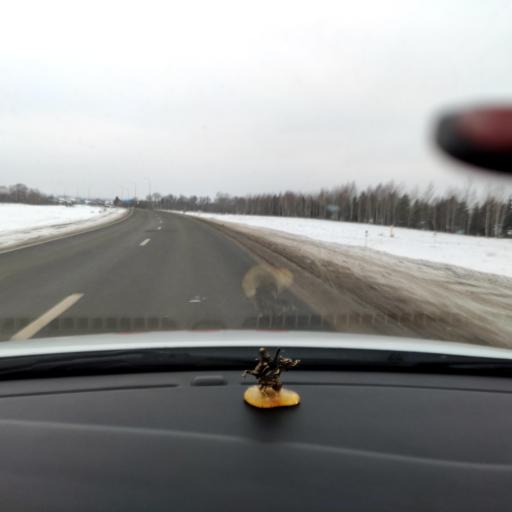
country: RU
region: Tatarstan
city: Stolbishchi
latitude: 55.6303
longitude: 49.2373
